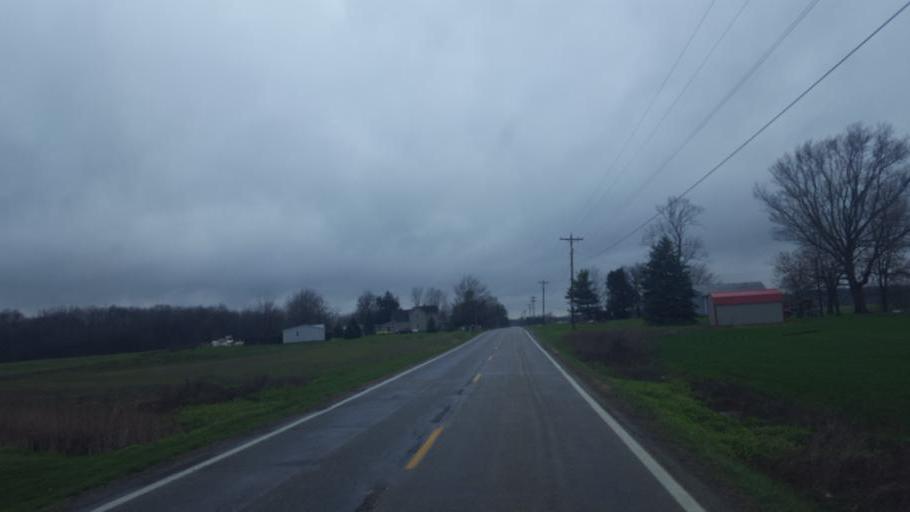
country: US
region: Ohio
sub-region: Morrow County
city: Cardington
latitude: 40.4884
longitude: -82.8605
